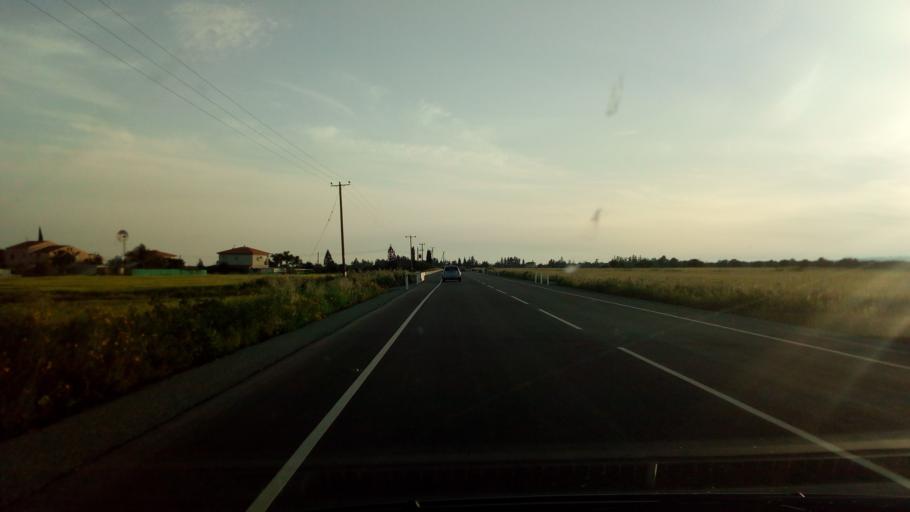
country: CY
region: Larnaka
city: Tersefanou
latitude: 34.8100
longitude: 33.5201
